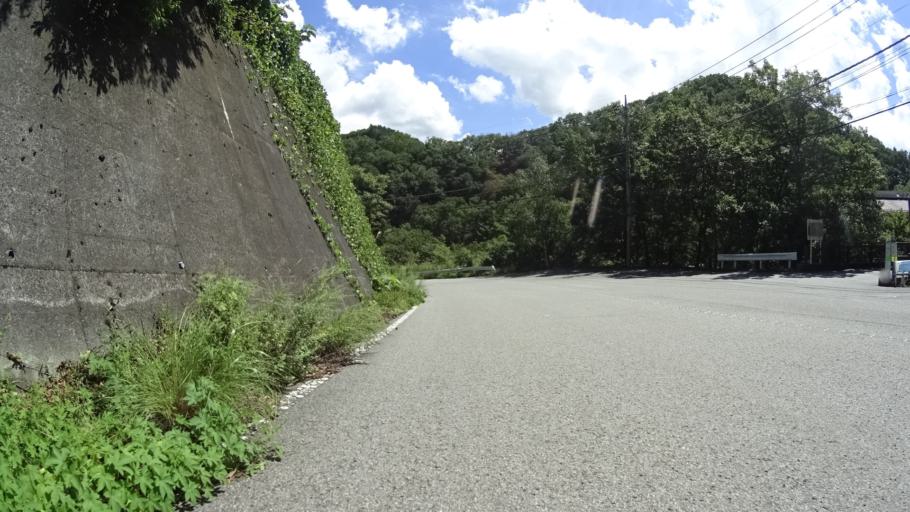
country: JP
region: Yamanashi
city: Enzan
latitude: 35.6583
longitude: 138.8152
